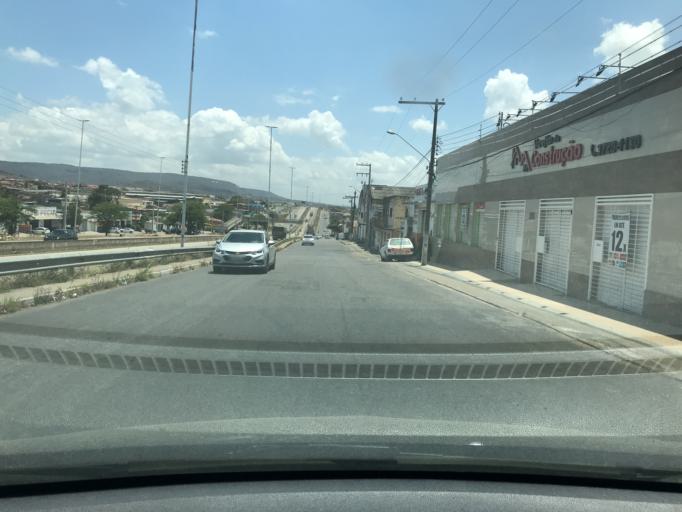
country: BR
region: Pernambuco
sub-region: Bezerros
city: Bezerros
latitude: -8.2431
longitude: -35.7528
